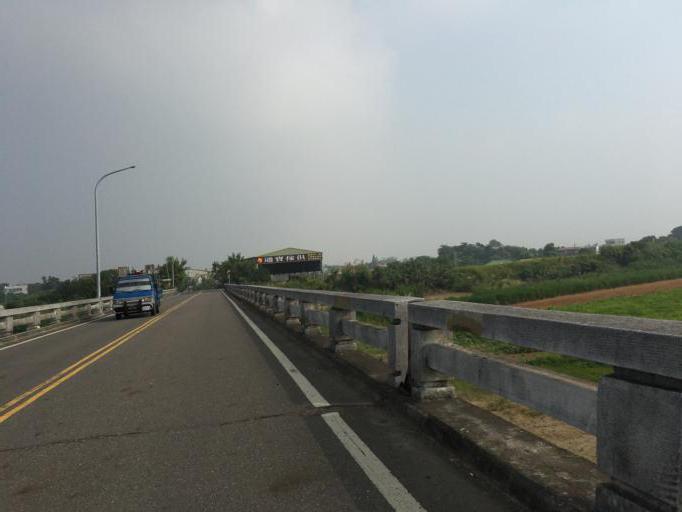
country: TW
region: Taiwan
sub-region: Chiayi
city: Taibao
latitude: 23.4829
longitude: 120.2931
